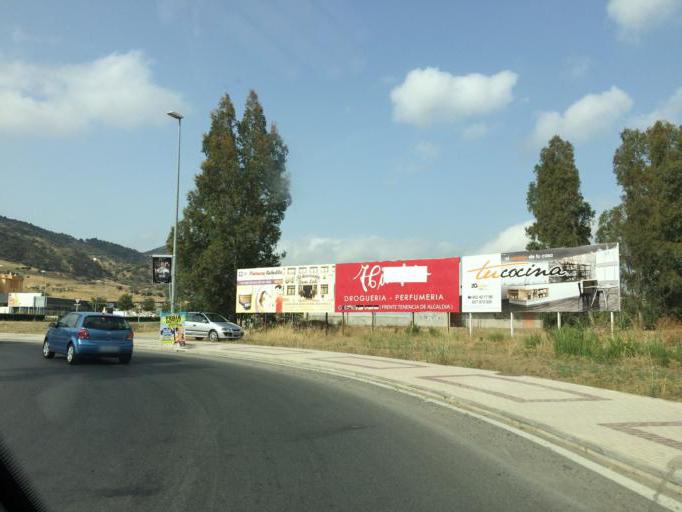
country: ES
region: Andalusia
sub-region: Provincia de Malaga
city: Estacion de Cartama
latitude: 36.7231
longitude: -4.6152
